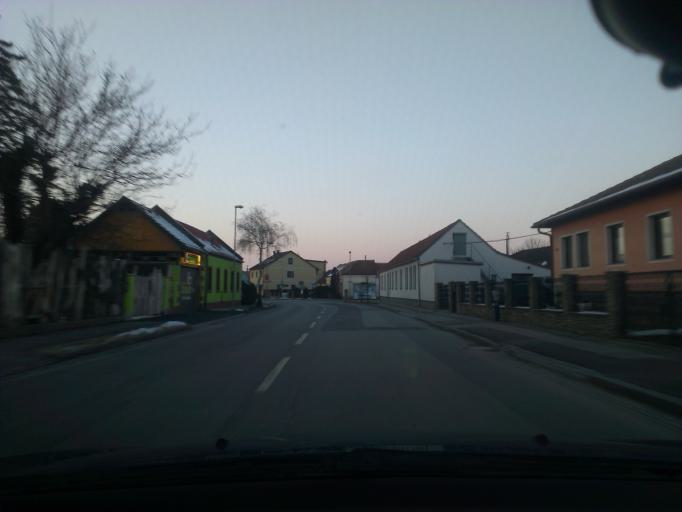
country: AT
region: Lower Austria
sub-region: Politischer Bezirk Bruck an der Leitha
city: Enzersdorf an der Fischa
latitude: 48.0780
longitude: 16.6081
